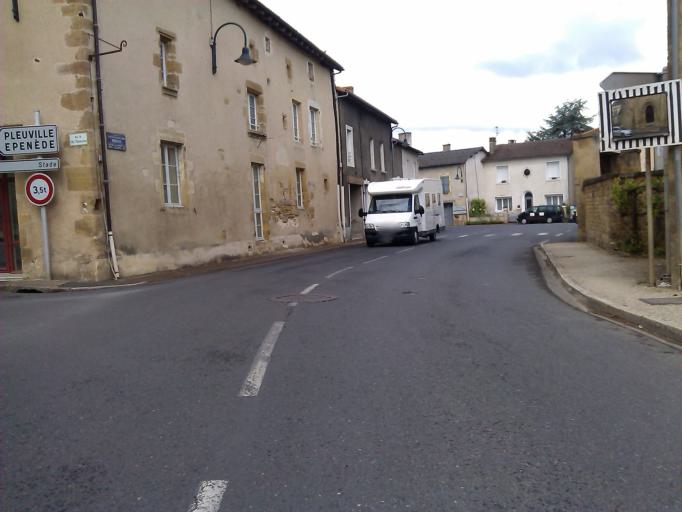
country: FR
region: Poitou-Charentes
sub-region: Departement de la Vienne
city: Availles-Limouzine
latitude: 46.1159
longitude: 0.5707
